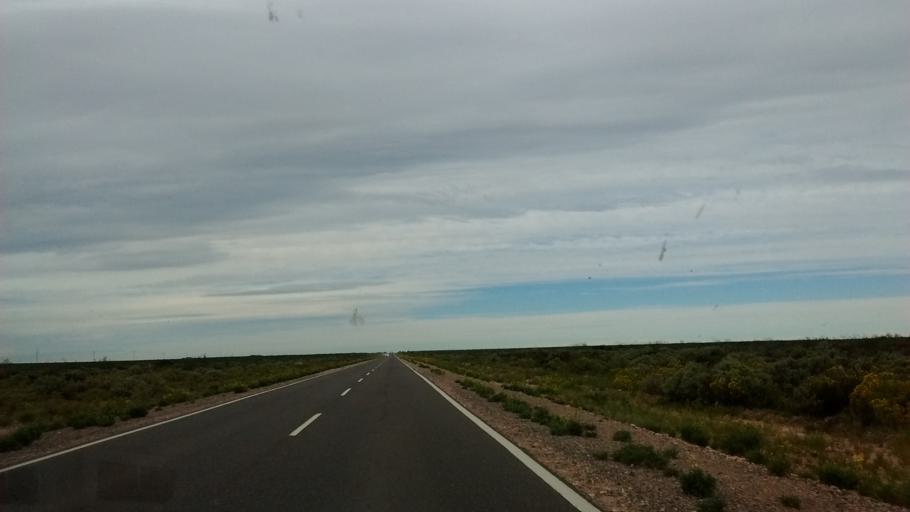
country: AR
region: Rio Negro
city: Contraalmirante Cordero
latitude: -38.3553
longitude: -68.0159
